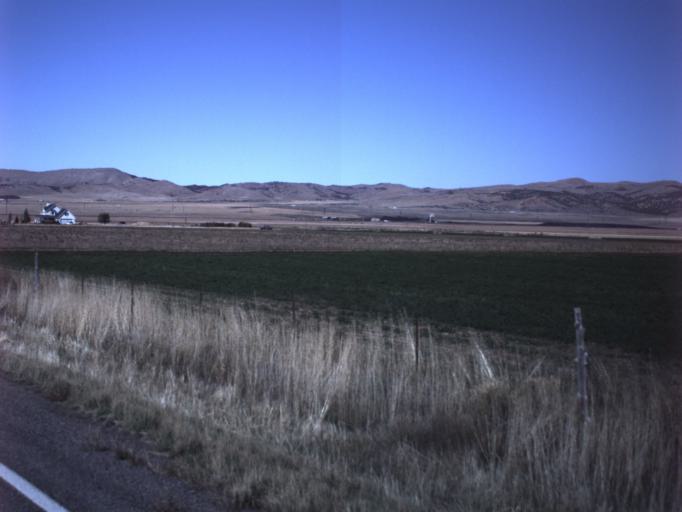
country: US
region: Utah
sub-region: Juab County
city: Nephi
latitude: 39.5581
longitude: -111.8874
